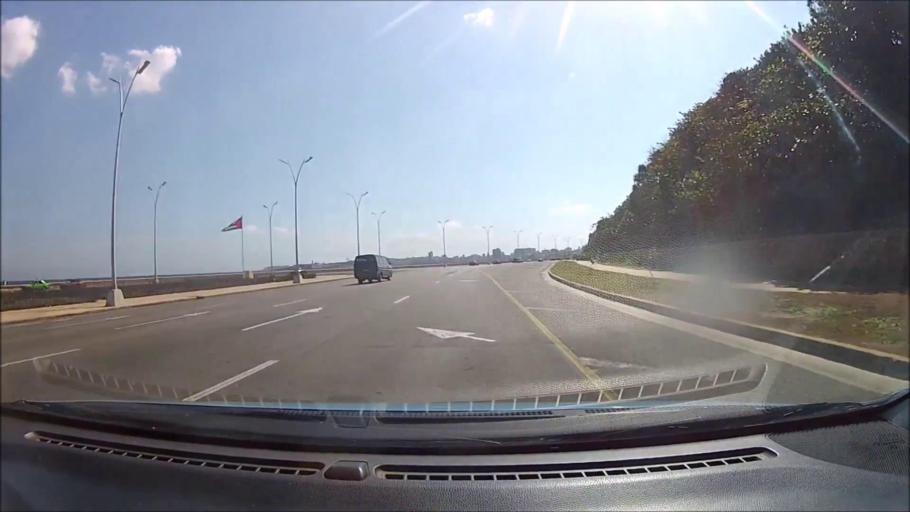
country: CU
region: La Habana
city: Havana
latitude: 23.1444
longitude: -82.3814
